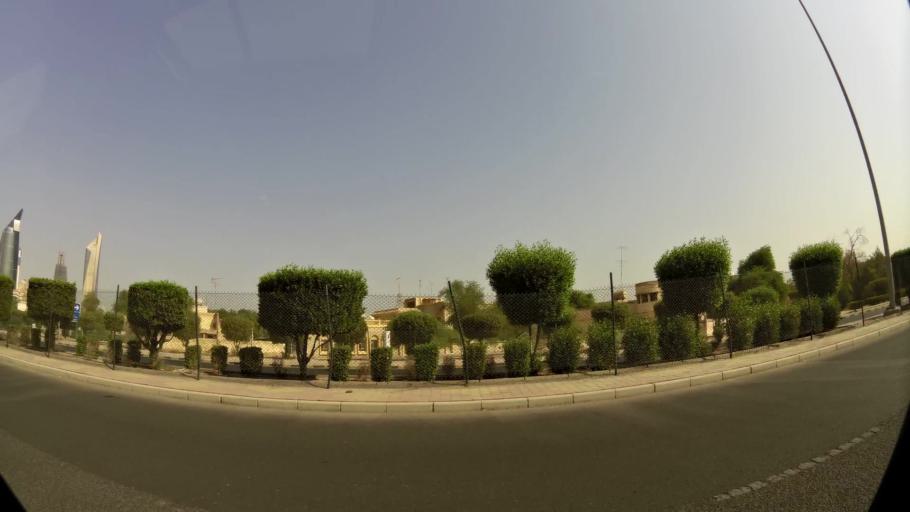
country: KW
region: Al Asimah
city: Ad Dasmah
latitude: 29.3624
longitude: 47.9956
